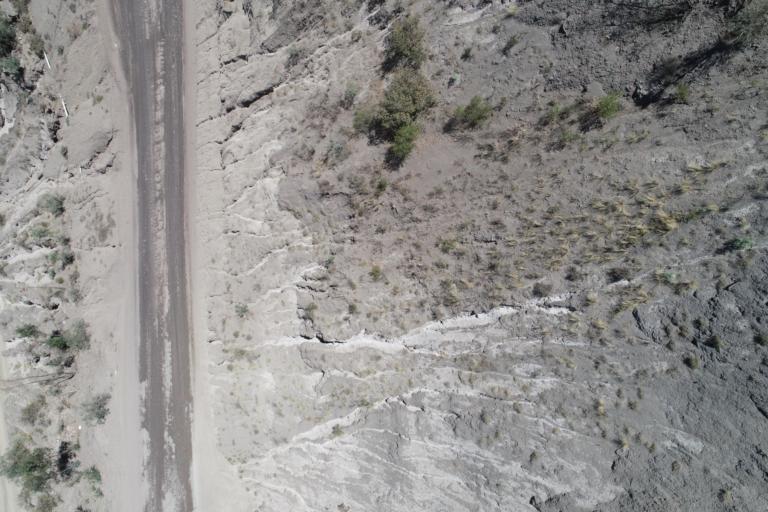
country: BO
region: La Paz
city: La Paz
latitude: -16.6141
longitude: -68.0593
